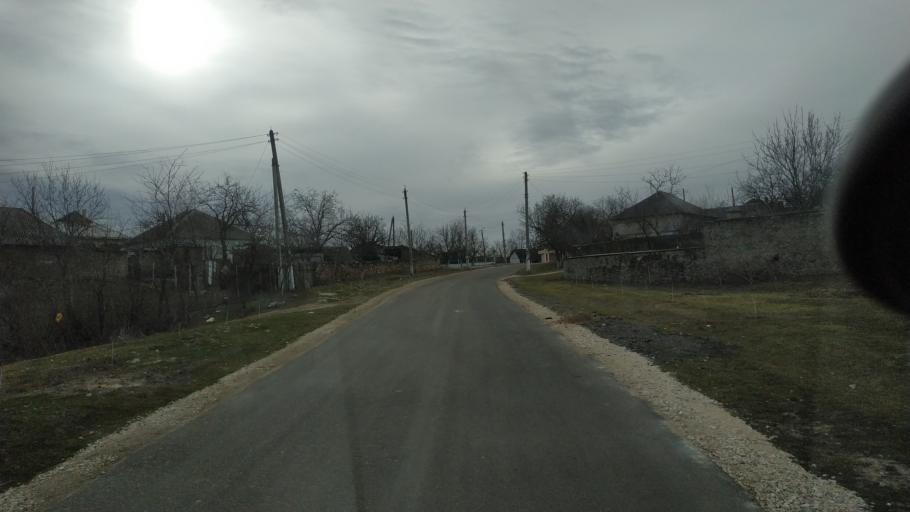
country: MD
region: Telenesti
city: Cocieri
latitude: 47.2596
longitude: 29.0594
